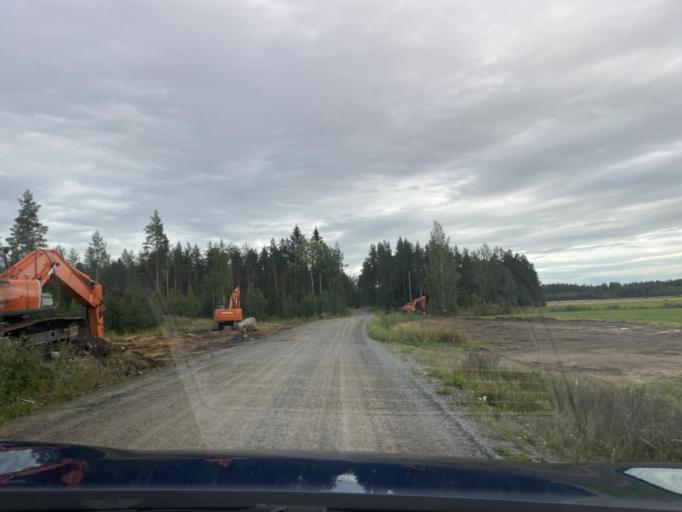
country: FI
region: Pirkanmaa
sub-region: Lounais-Pirkanmaa
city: Punkalaidun
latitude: 61.2506
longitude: 23.0339
